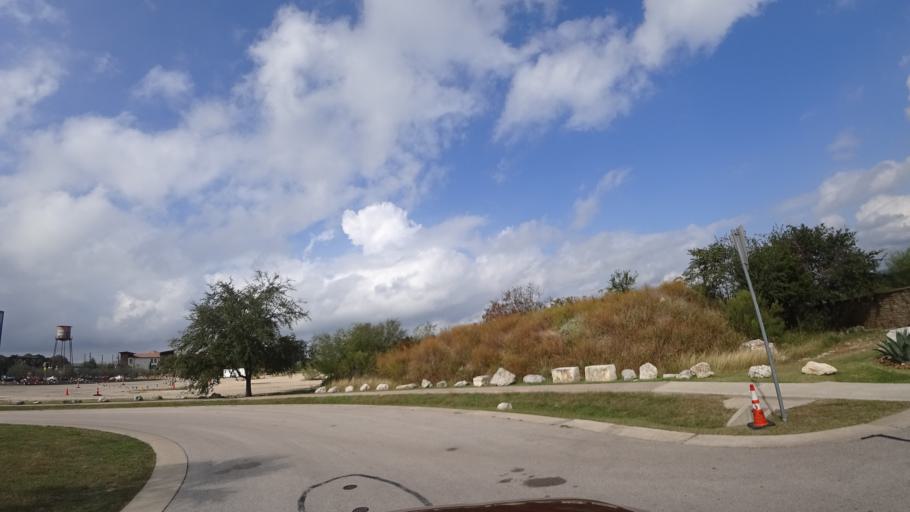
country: US
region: Texas
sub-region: Travis County
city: Hudson Bend
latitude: 30.4056
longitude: -97.8716
